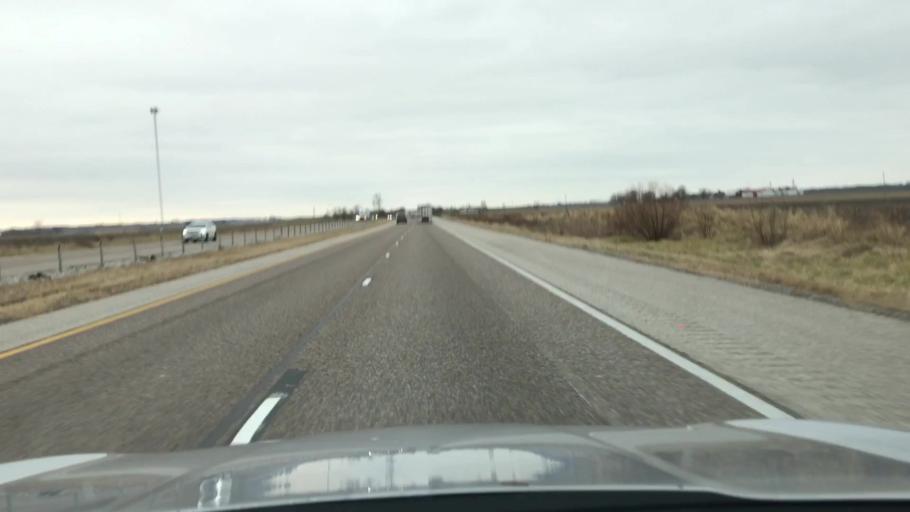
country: US
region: Illinois
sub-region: Madison County
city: Edwardsville
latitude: 38.8384
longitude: -89.8739
